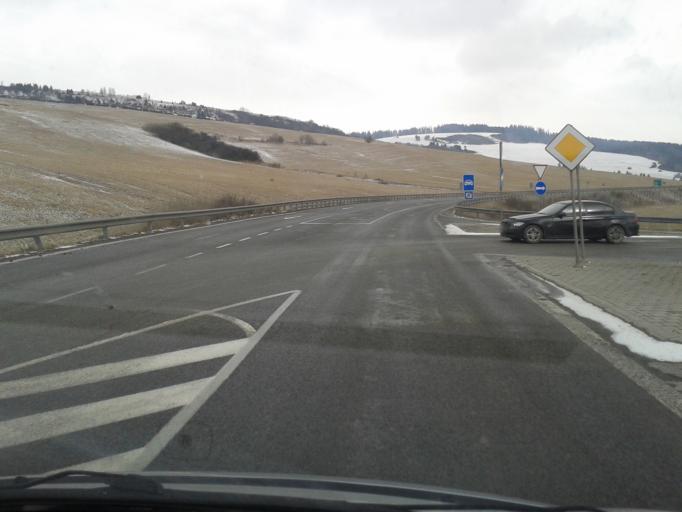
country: SK
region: Zilinsky
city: Tvrdosin
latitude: 49.3436
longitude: 19.5683
